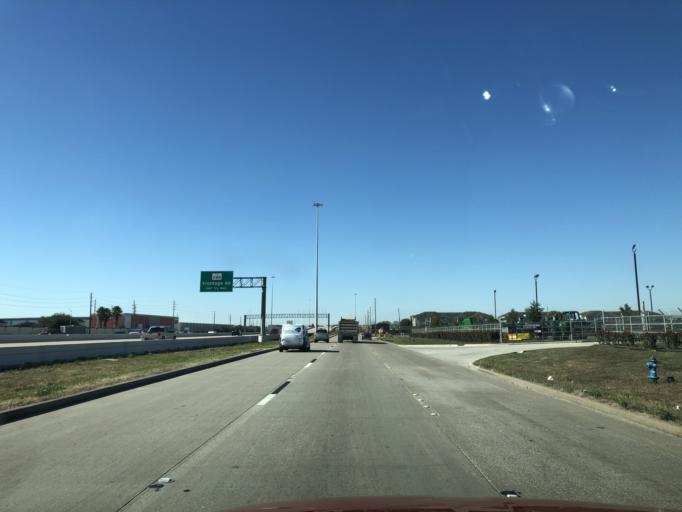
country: US
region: Texas
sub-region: Brazoria County
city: Brookside Village
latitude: 29.5986
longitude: -95.3597
